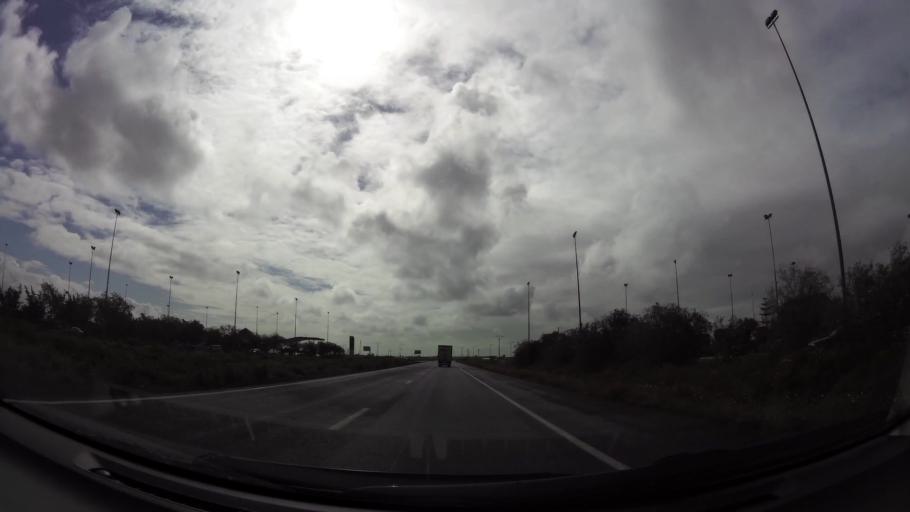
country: MA
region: Grand Casablanca
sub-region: Nouaceur
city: Dar Bouazza
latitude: 33.3534
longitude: -7.9788
